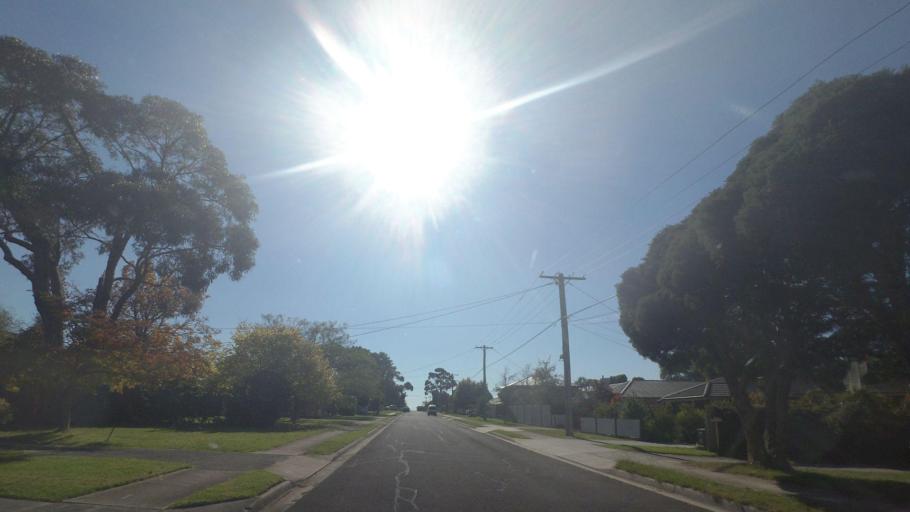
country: AU
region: Victoria
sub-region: Knox
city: Ferntree Gully
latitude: -37.8814
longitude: 145.2818
